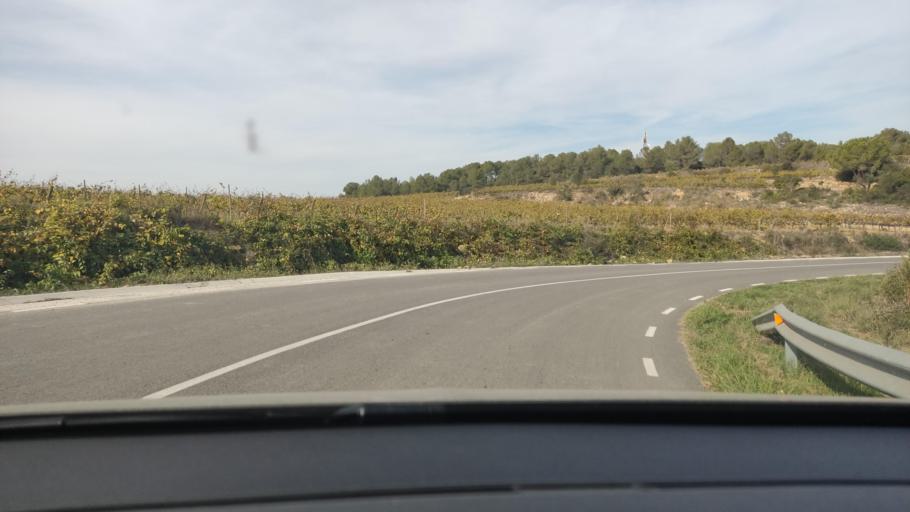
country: ES
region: Catalonia
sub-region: Provincia de Barcelona
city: Subirats
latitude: 41.4055
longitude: 1.8093
